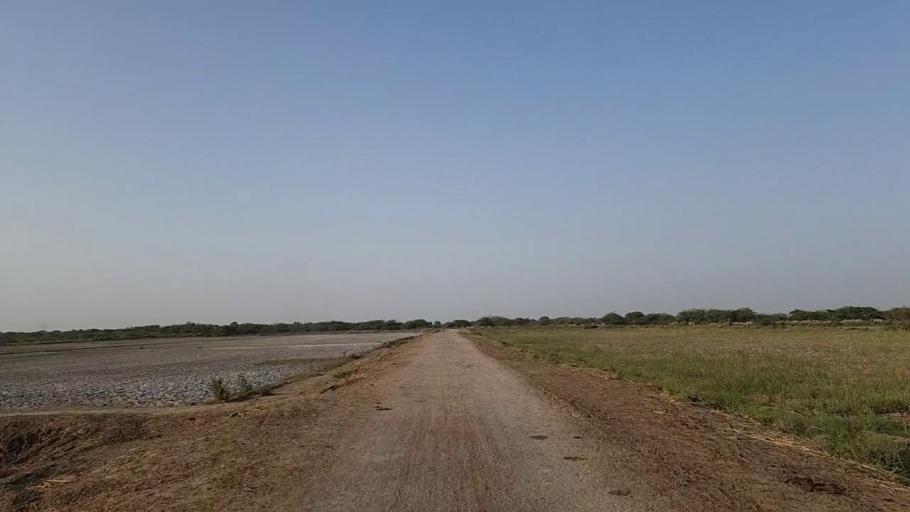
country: PK
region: Sindh
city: Jati
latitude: 24.3808
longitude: 68.1482
